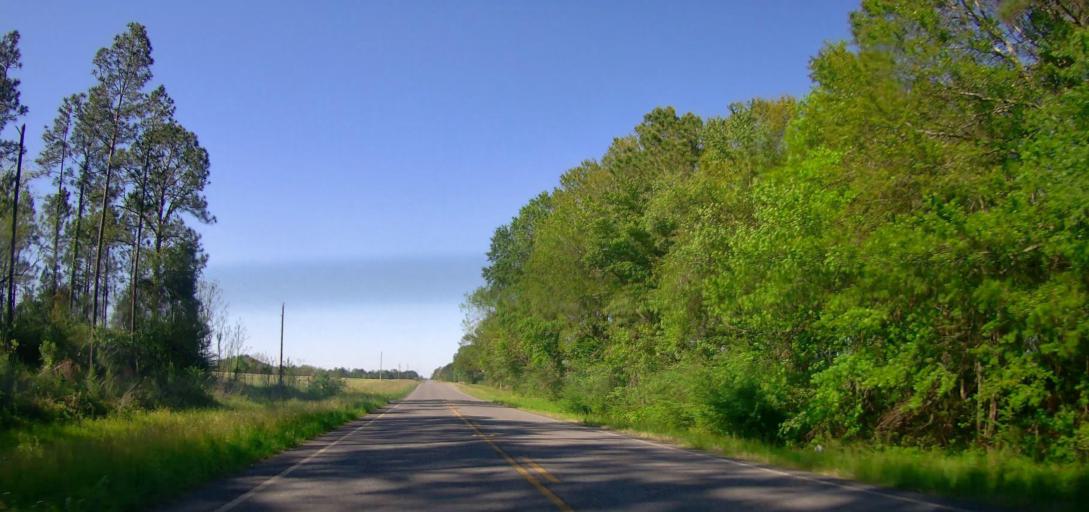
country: US
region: Georgia
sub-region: Wilcox County
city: Rochelle
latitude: 32.0516
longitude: -83.5036
